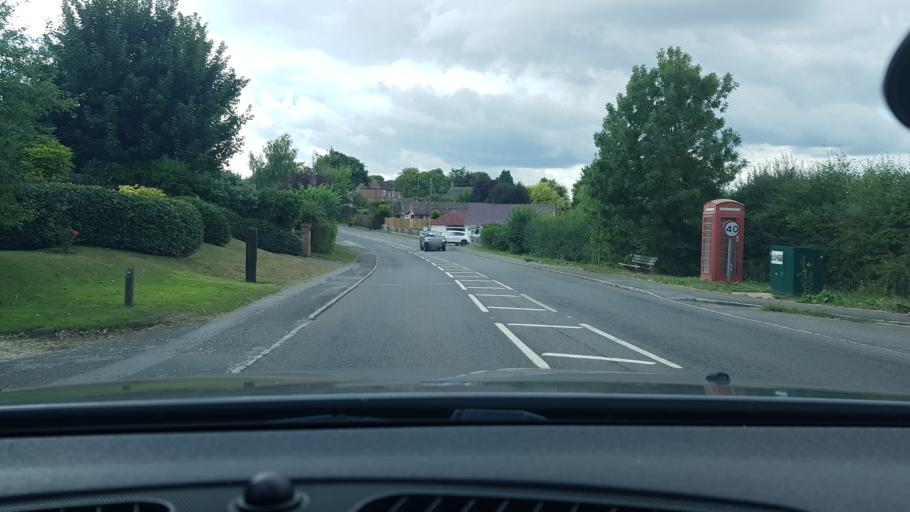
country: GB
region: England
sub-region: West Berkshire
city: Wickham
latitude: 51.4434
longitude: -1.4311
